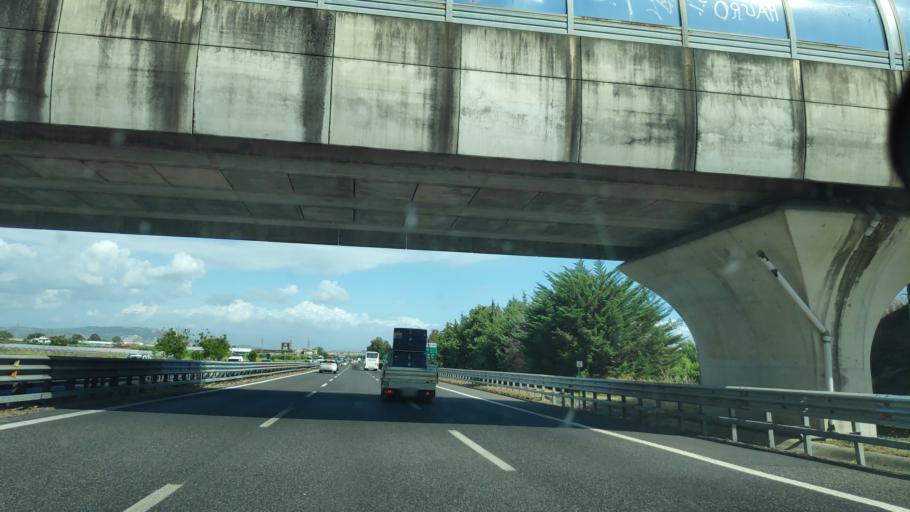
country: IT
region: Campania
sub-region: Provincia di Salerno
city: Sant'Antonio
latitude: 40.6425
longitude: 14.8955
